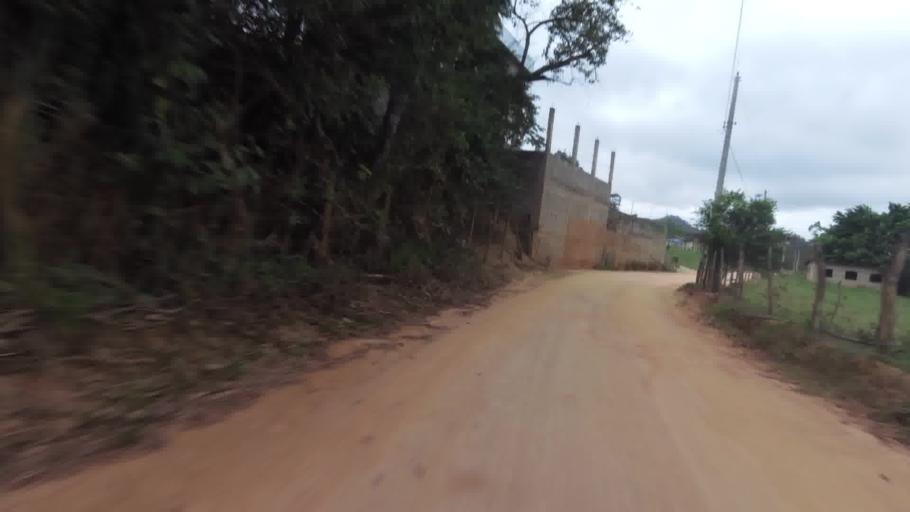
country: BR
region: Espirito Santo
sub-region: Alfredo Chaves
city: Alfredo Chaves
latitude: -20.6934
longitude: -40.7116
